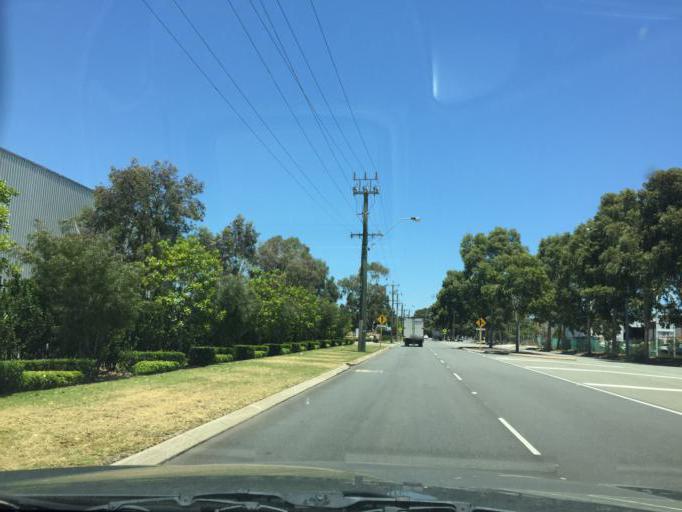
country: AU
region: Western Australia
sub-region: Canning
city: Canning Vale
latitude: -32.0608
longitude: 115.9302
